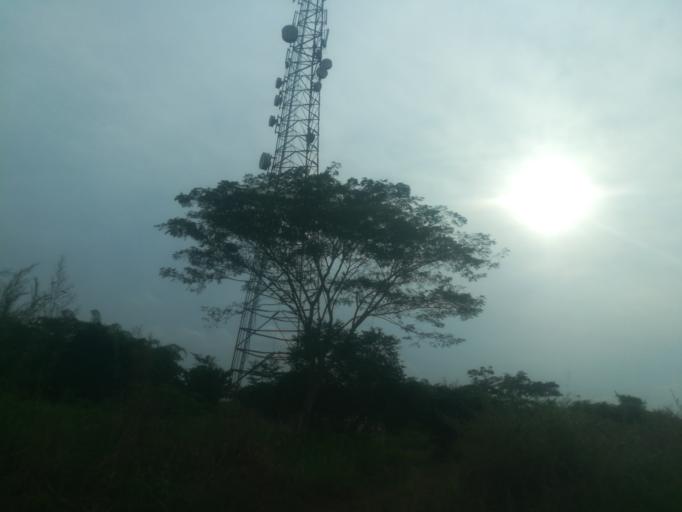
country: NG
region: Ogun
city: Ayetoro
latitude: 7.2414
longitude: 3.1251
